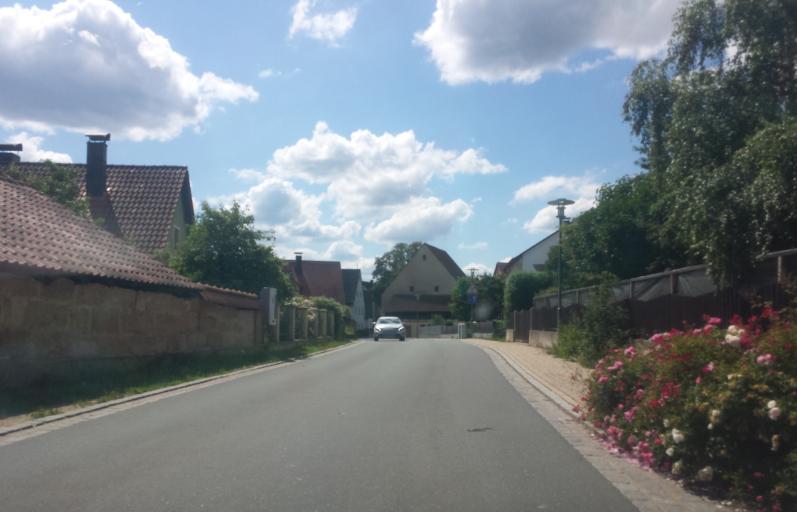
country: DE
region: Bavaria
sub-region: Upper Franconia
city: Hallerndorf
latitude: 49.7797
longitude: 10.9564
